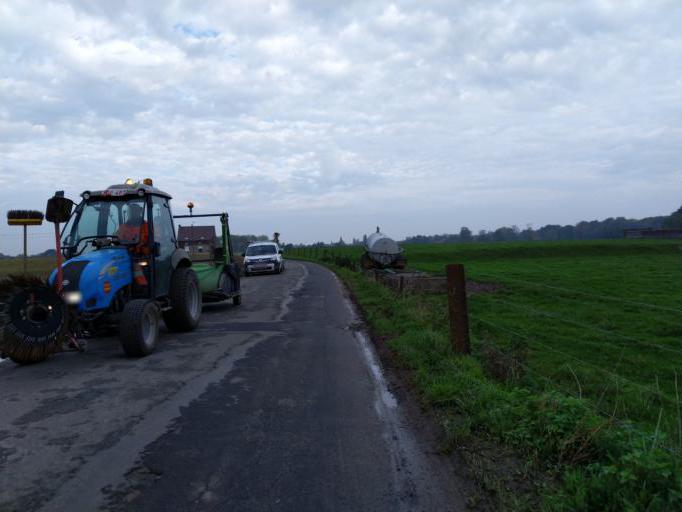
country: BE
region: Wallonia
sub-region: Province du Hainaut
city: Brugelette
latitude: 50.6004
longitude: 3.8430
